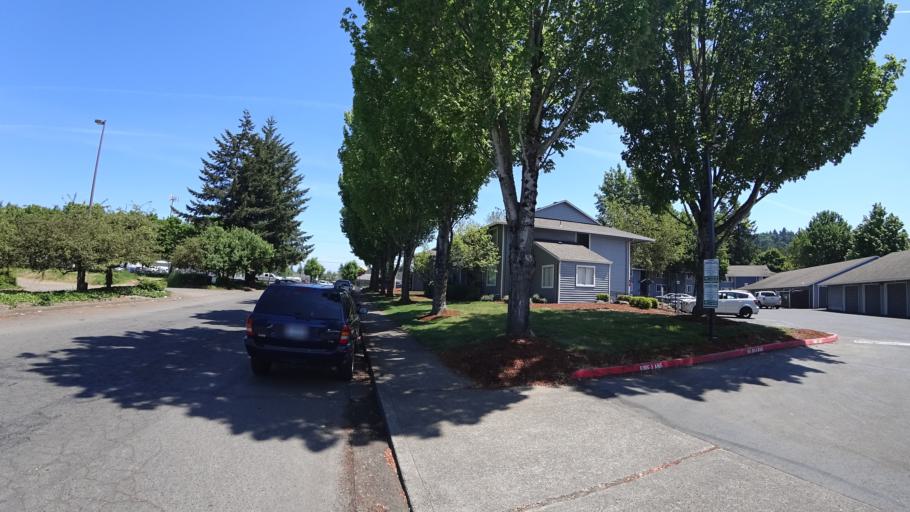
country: US
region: Oregon
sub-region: Multnomah County
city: Gresham
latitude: 45.4904
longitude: -122.4858
